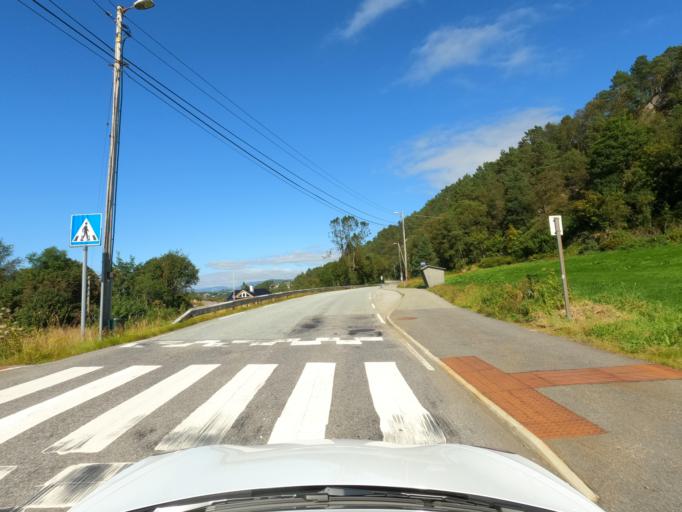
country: NO
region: Hordaland
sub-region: Bergen
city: Sandsli
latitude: 60.2371
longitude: 5.3003
